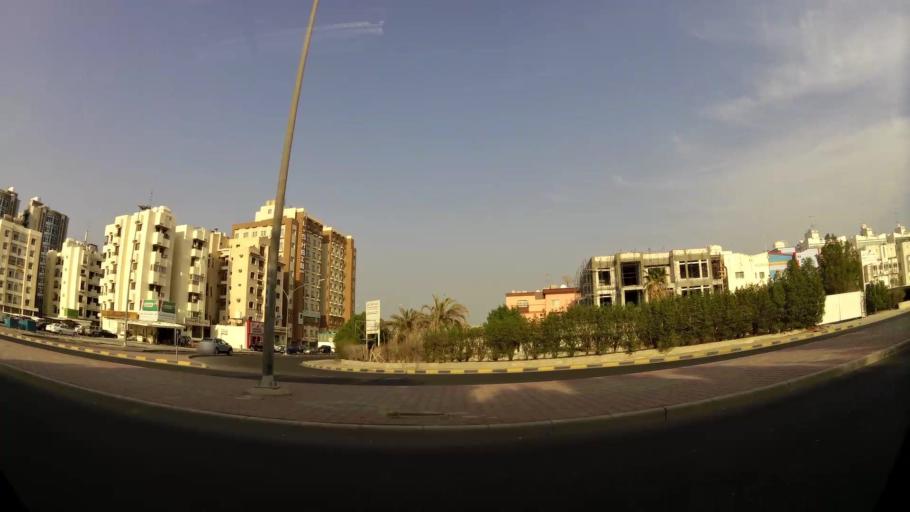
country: KW
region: Muhafazat Hawalli
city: Hawalli
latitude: 29.3169
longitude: 48.0178
